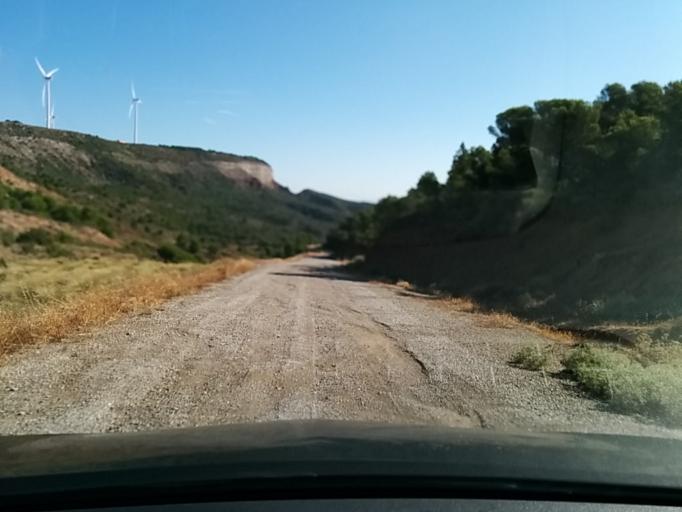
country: ES
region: Aragon
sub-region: Provincia de Zaragoza
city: Novillas
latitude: 42.0206
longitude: -1.3164
